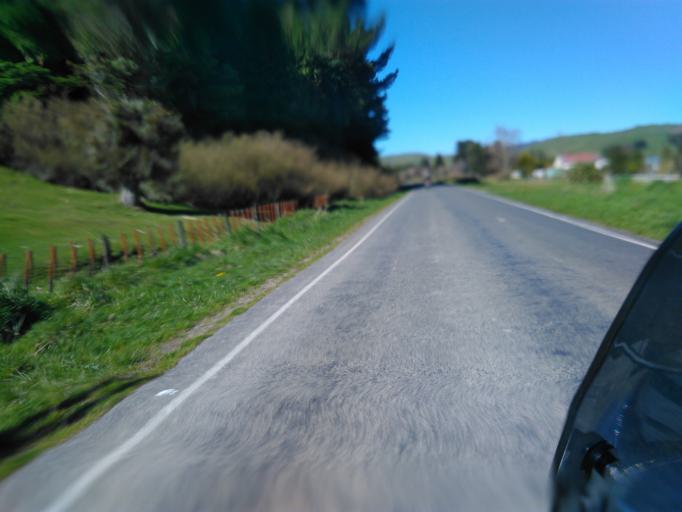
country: NZ
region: Bay of Plenty
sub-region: Opotiki District
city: Opotiki
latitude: -38.3493
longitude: 177.5324
